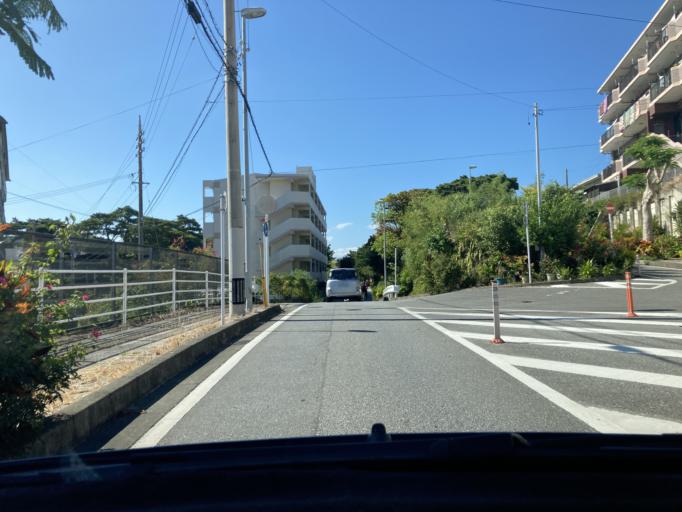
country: JP
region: Okinawa
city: Naha-shi
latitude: 26.2374
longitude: 127.7009
